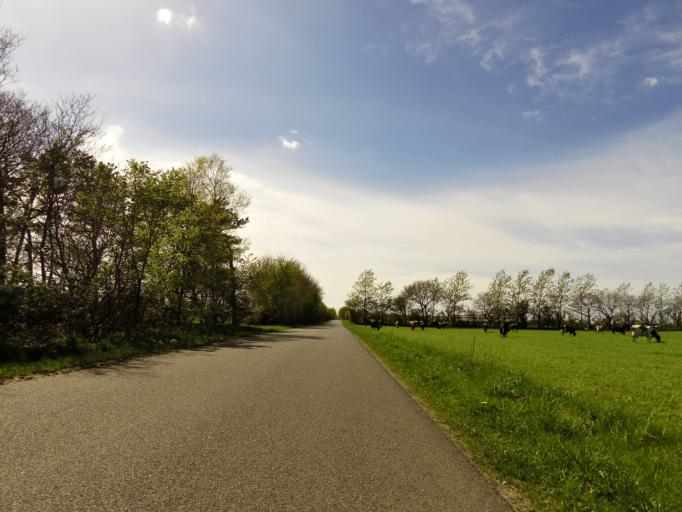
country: DK
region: Central Jutland
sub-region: Skive Kommune
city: Skive
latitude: 56.4601
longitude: 8.9715
